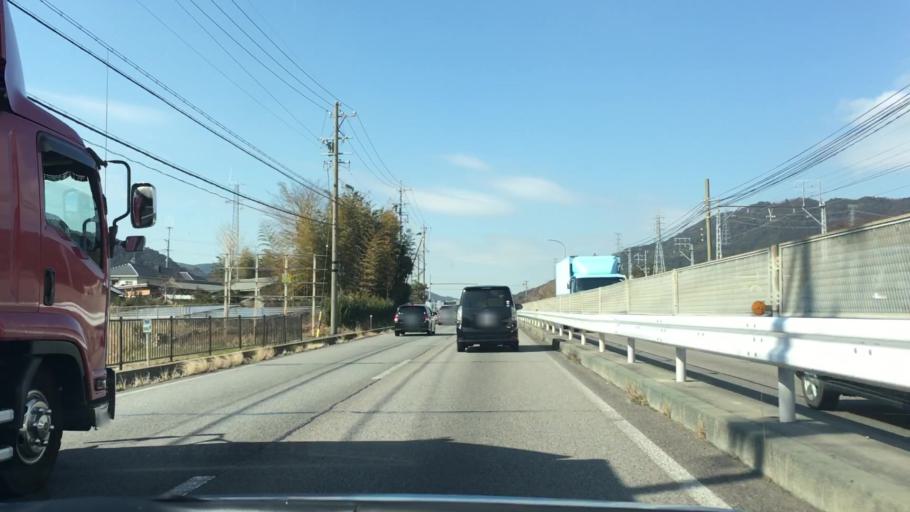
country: JP
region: Aichi
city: Gamagori
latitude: 34.8647
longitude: 137.3015
